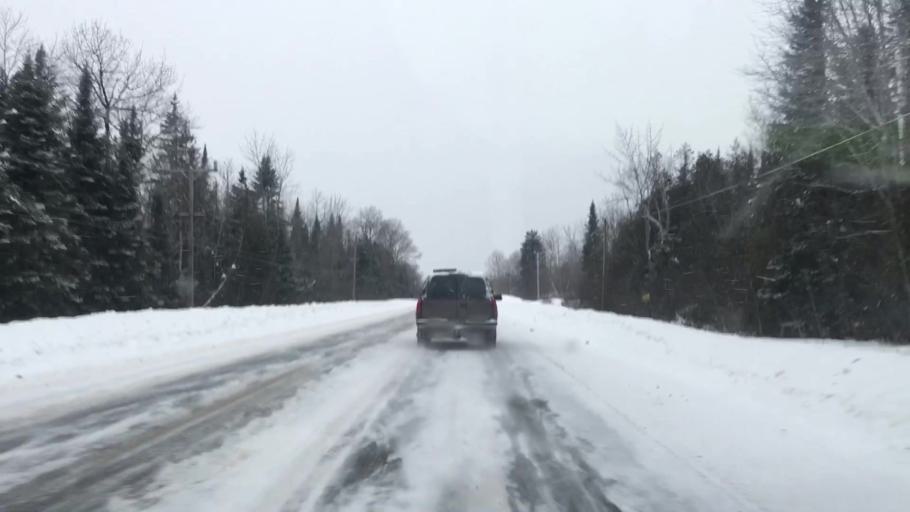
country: US
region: Maine
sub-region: Penobscot County
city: Medway
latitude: 45.5877
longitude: -68.4374
